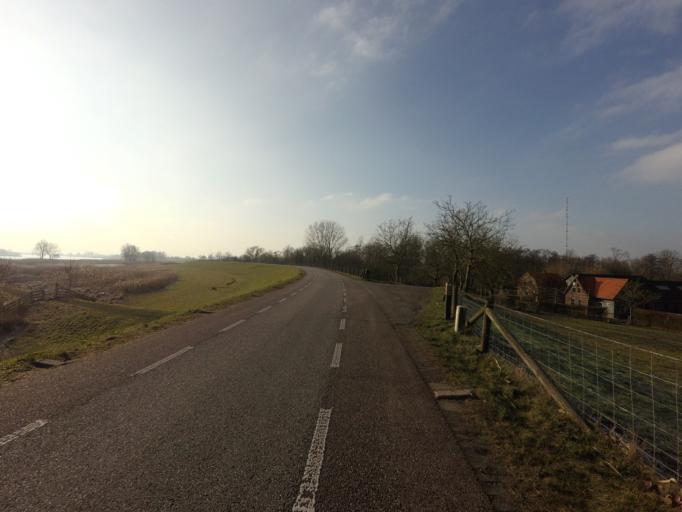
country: NL
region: Utrecht
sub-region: Gemeente Lopik
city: Lopik
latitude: 51.9671
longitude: 4.9396
